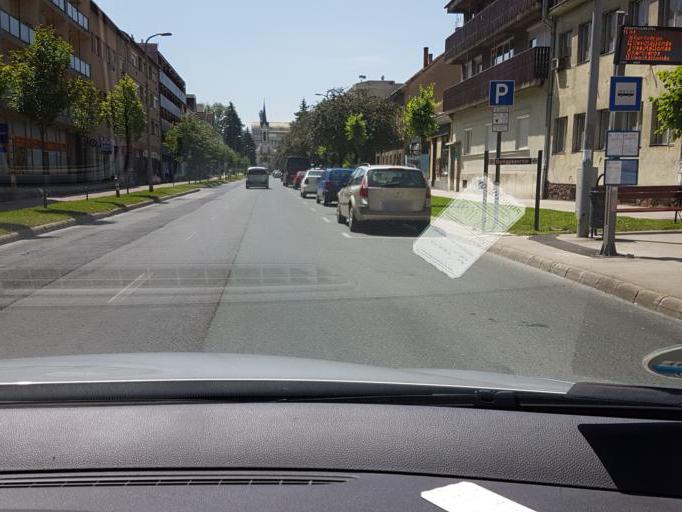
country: HU
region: Zala
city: Zalaegerszeg
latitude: 46.8391
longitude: 16.8458
